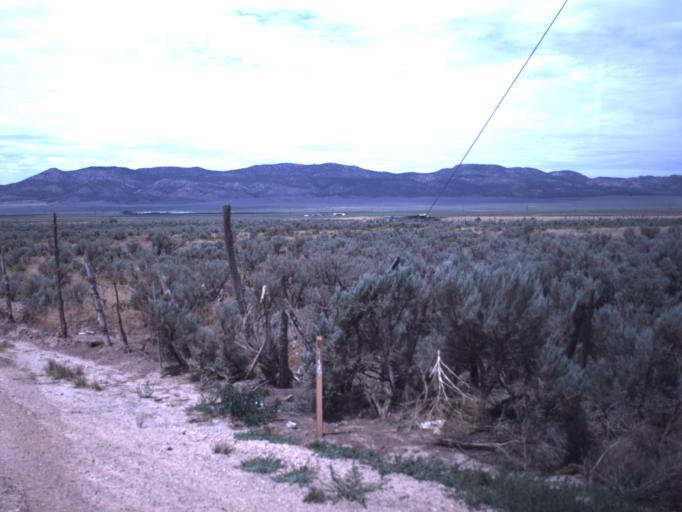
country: US
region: Utah
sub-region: Iron County
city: Parowan
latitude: 37.9117
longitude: -112.7795
